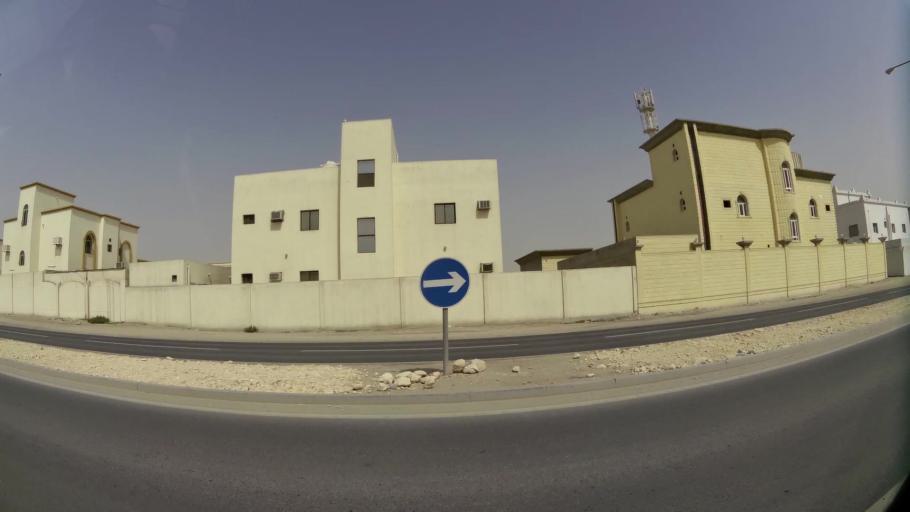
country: QA
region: Baladiyat ar Rayyan
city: Ar Rayyan
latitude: 25.2369
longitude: 51.3821
